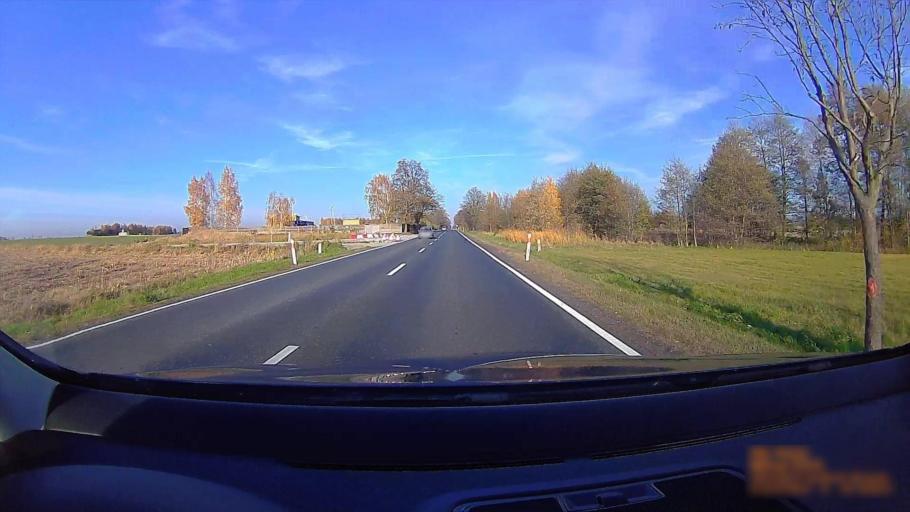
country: PL
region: Greater Poland Voivodeship
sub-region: Powiat koninski
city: Stare Miasto
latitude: 52.1307
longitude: 18.1809
